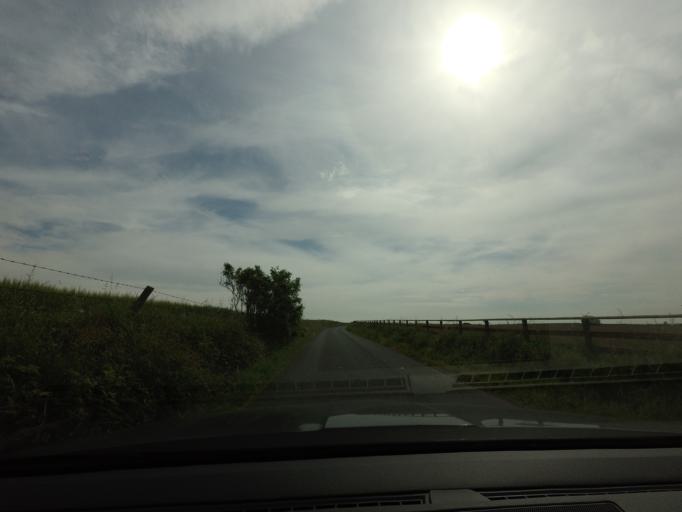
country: GB
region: Scotland
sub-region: Aberdeenshire
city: Turriff
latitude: 57.5350
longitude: -2.4286
